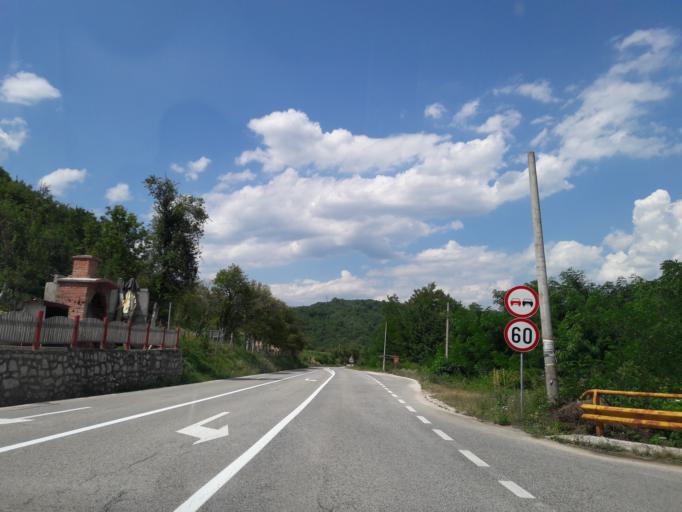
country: BA
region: Republika Srpska
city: Mrkonjic Grad
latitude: 44.5357
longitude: 17.1494
